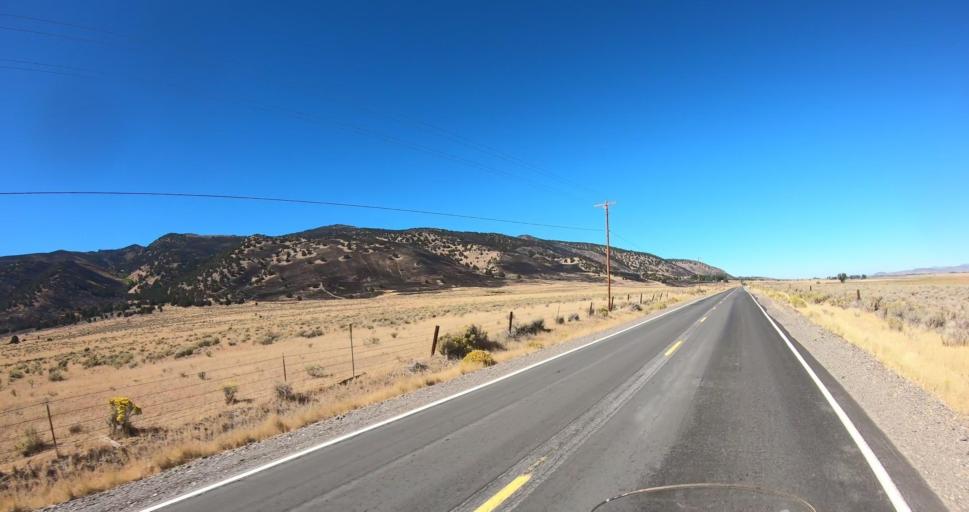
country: US
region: Oregon
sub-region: Lake County
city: Lakeview
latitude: 42.6279
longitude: -120.5103
